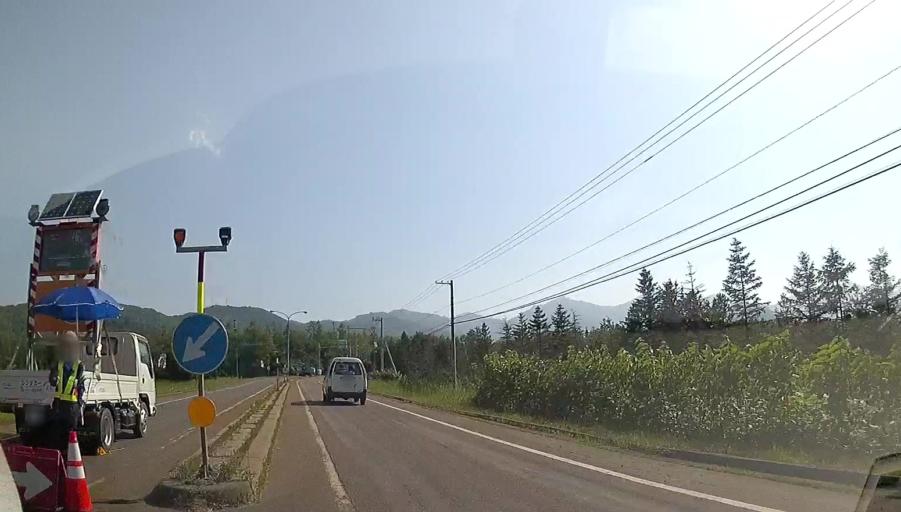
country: JP
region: Hokkaido
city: Otofuke
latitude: 42.9846
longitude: 142.8380
